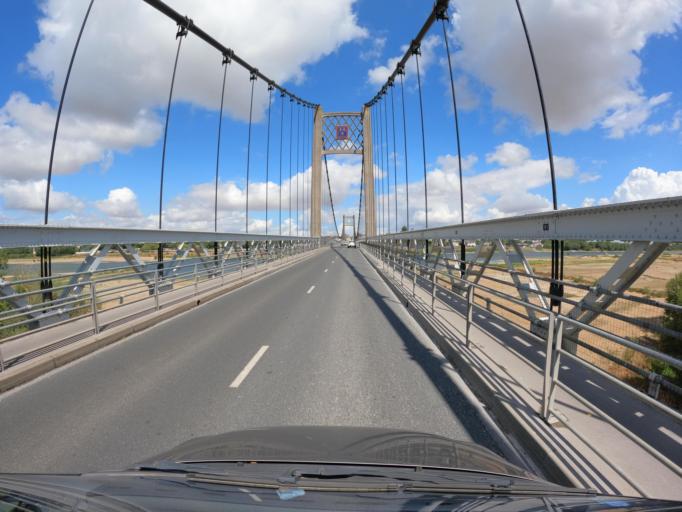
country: FR
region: Pays de la Loire
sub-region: Departement de la Loire-Atlantique
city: Ancenis
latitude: 47.3604
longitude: -1.1757
